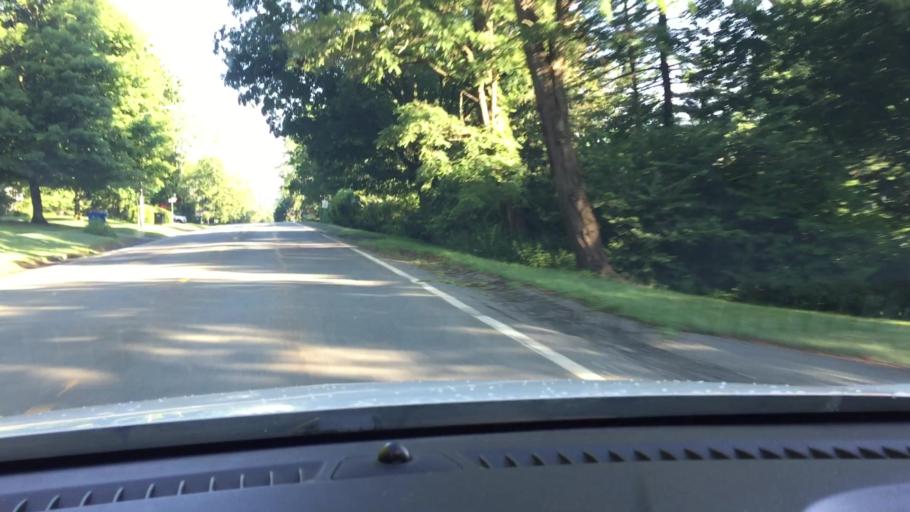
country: US
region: Massachusetts
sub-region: Berkshire County
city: Lenox
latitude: 42.3535
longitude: -73.2790
